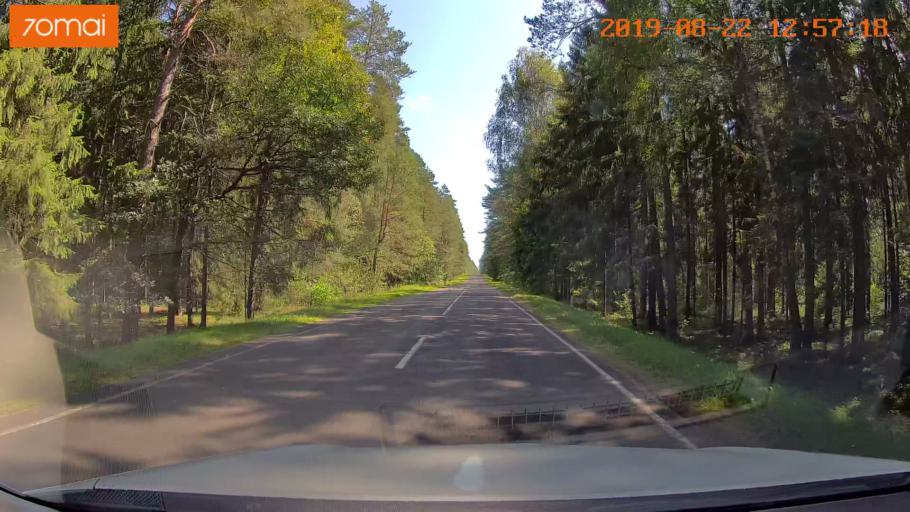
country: BY
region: Minsk
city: Prawdzinski
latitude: 53.4297
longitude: 27.7455
